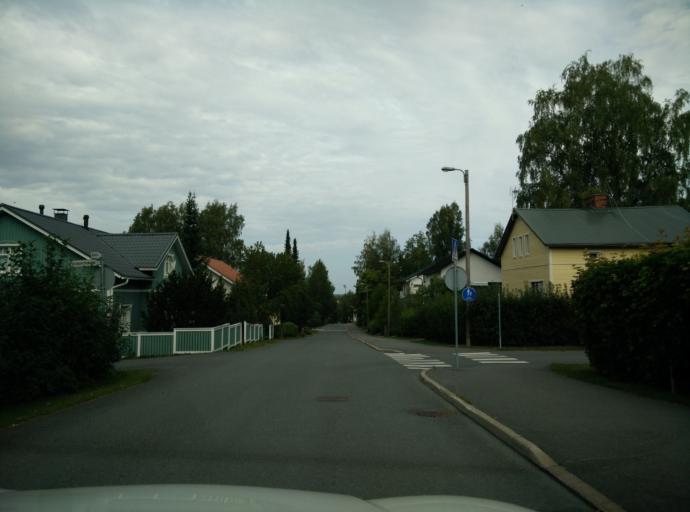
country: FI
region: Haeme
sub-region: Haemeenlinna
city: Haemeenlinna
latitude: 60.9895
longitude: 24.4467
